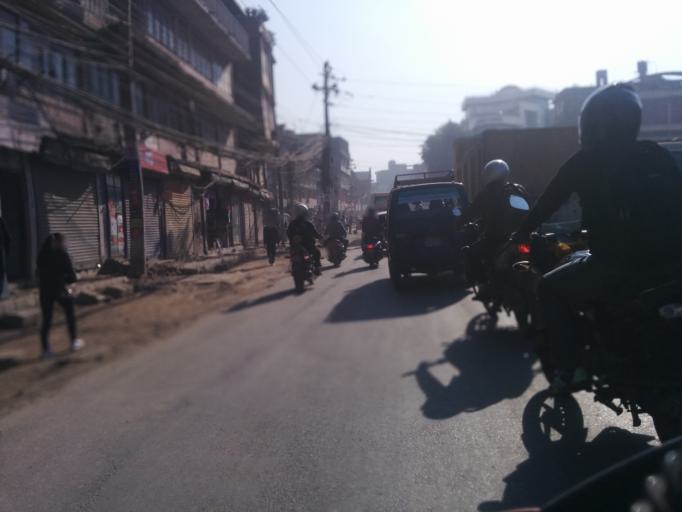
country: NP
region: Central Region
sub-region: Bagmati Zone
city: Kathmandu
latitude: 27.6975
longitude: 85.3040
